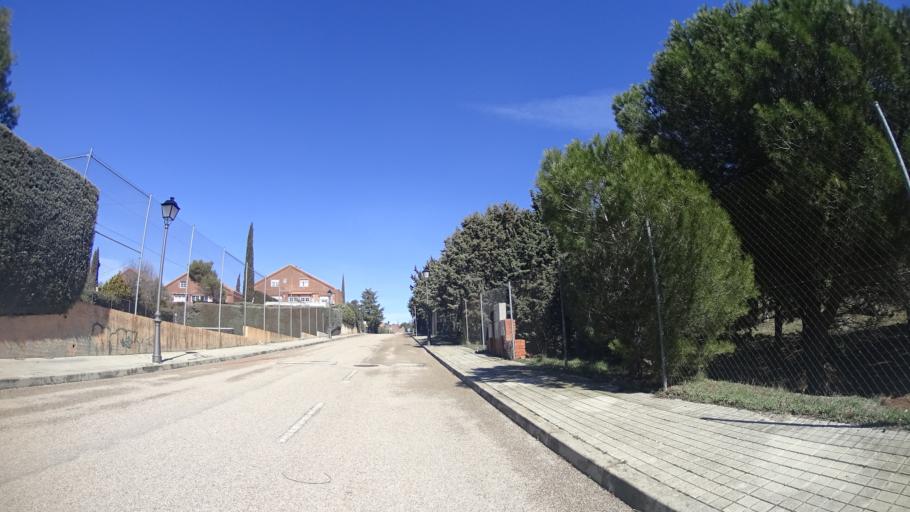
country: ES
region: Madrid
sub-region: Provincia de Madrid
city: Torrelodones
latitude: 40.5765
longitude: -3.9205
